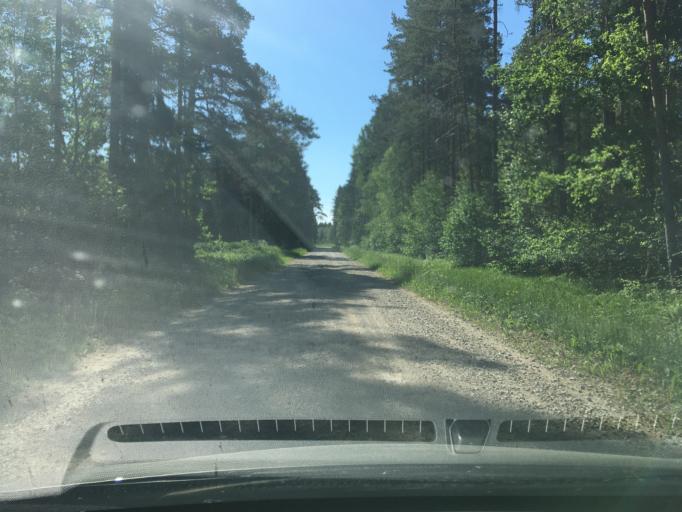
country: EE
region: Laeaene
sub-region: Lihula vald
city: Lihula
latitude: 58.6359
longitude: 23.7967
